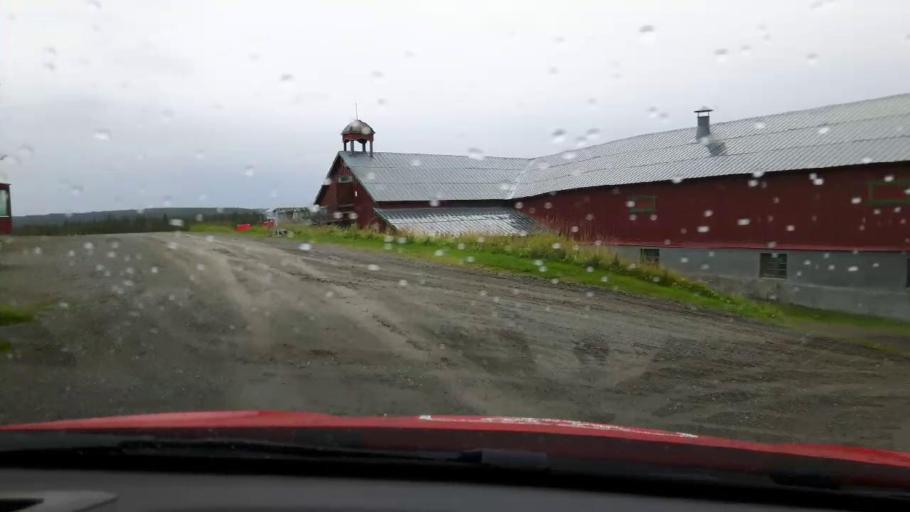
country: NO
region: Nord-Trondelag
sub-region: Meraker
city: Meraker
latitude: 63.5746
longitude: 12.2760
